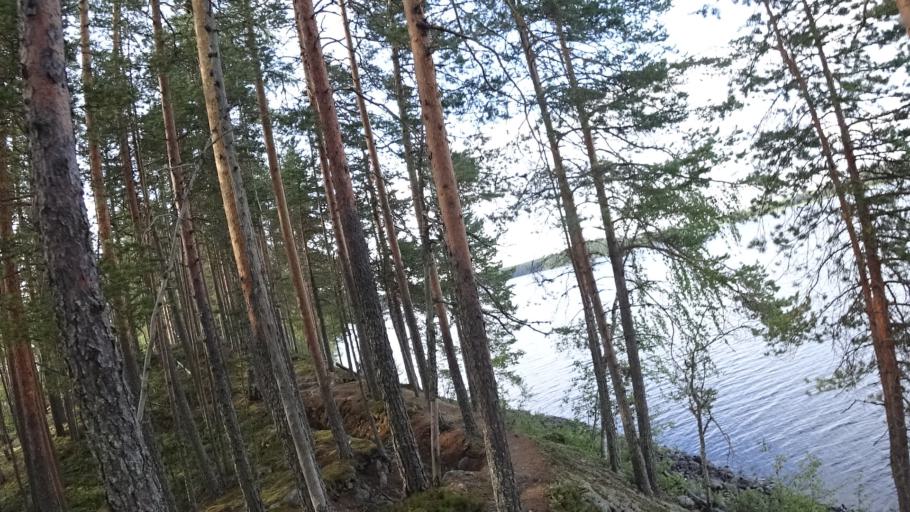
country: FI
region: North Karelia
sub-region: Joensuu
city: Ilomantsi
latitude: 62.5672
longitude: 31.1824
